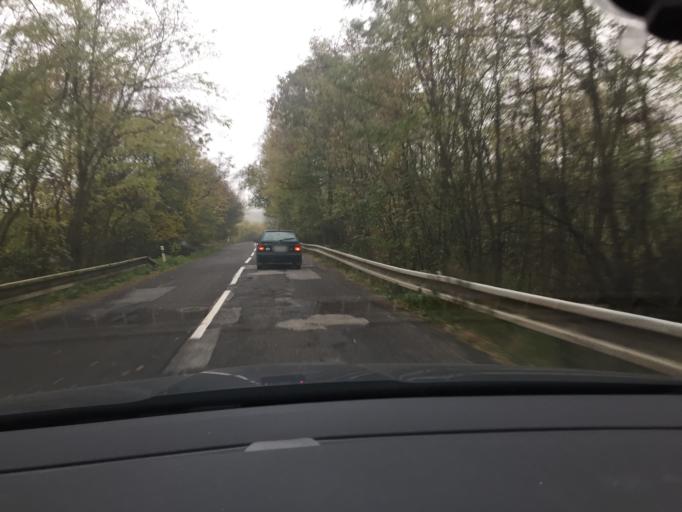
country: SK
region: Banskobystricky
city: Dudince
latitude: 48.1583
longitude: 18.9238
